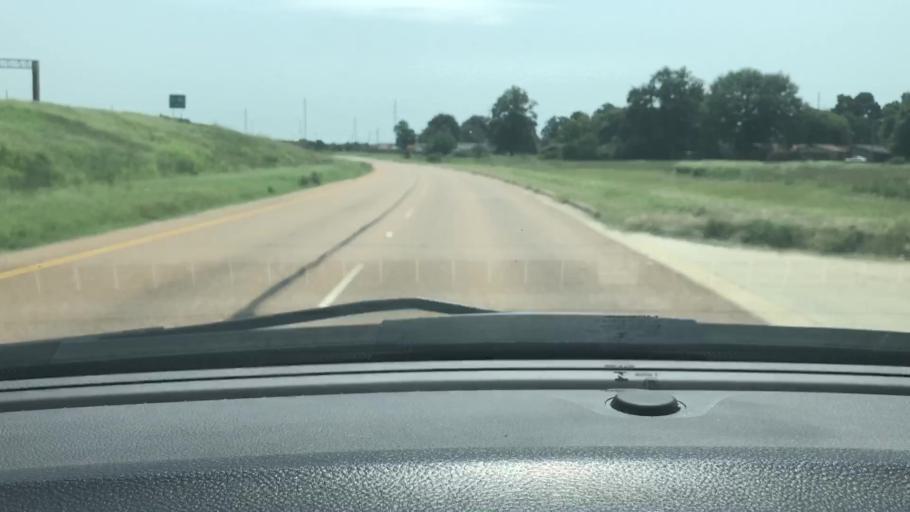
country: US
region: Texas
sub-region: Bowie County
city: Wake Village
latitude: 33.3880
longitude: -94.0956
